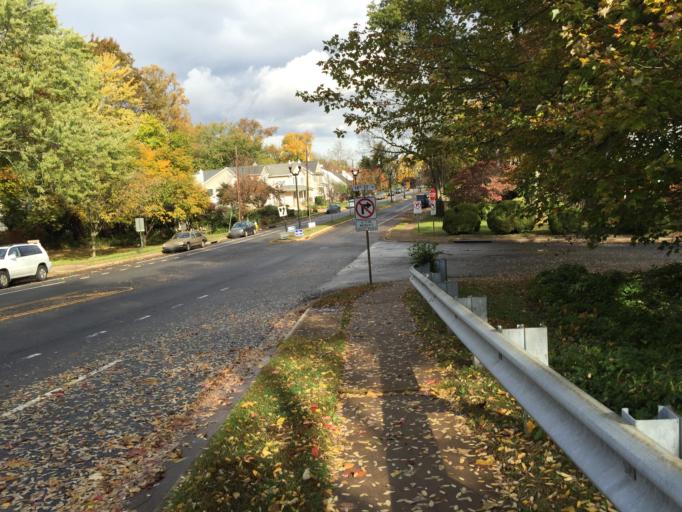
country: US
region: Virginia
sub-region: Fairfax County
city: Seven Corners
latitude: 38.8833
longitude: -77.1463
